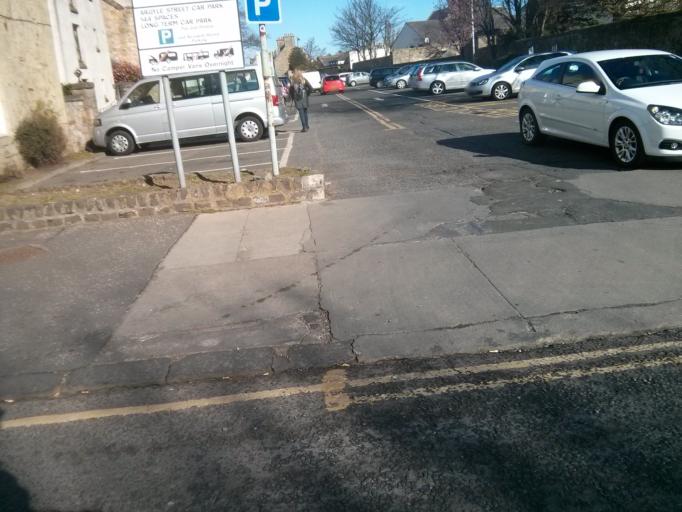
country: GB
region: Scotland
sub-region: Fife
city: Saint Andrews
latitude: 56.3385
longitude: -2.8022
